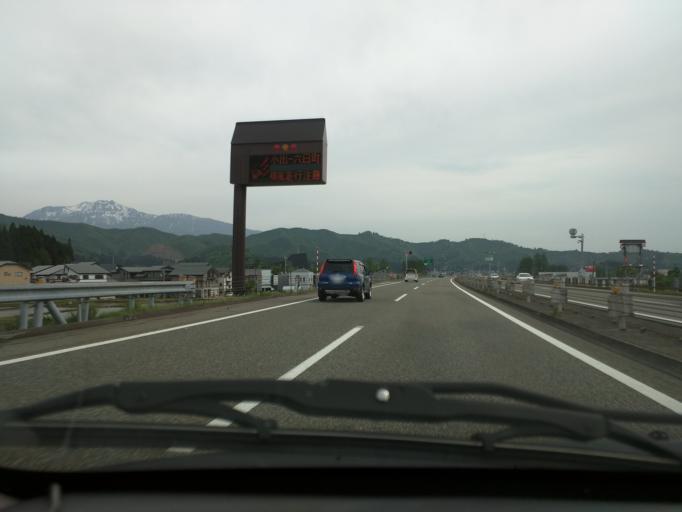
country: JP
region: Niigata
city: Muikamachi
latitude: 37.2197
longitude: 138.9765
